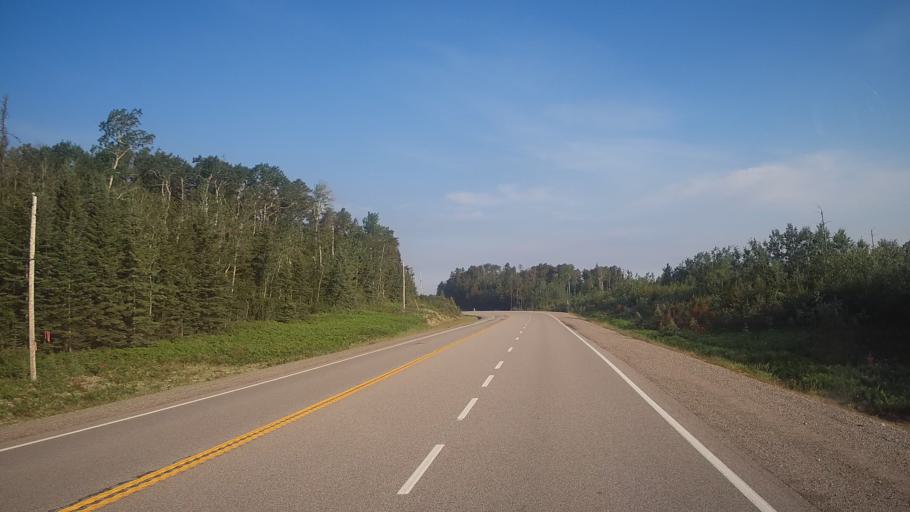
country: CA
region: Ontario
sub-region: Rainy River District
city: Atikokan
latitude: 49.3686
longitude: -91.5584
